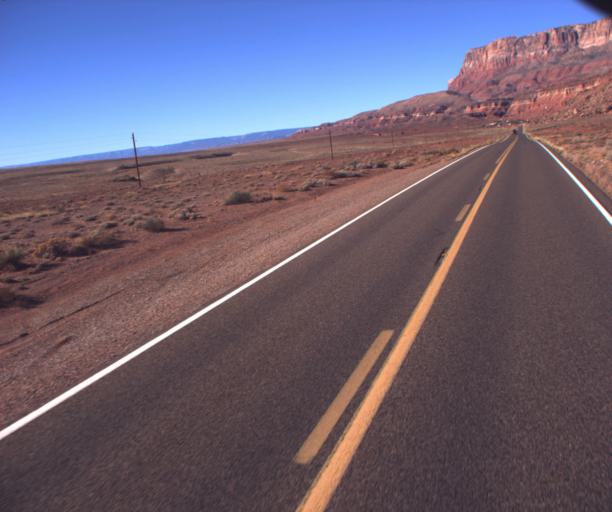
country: US
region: Arizona
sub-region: Coconino County
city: Page
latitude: 36.7499
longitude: -111.7322
